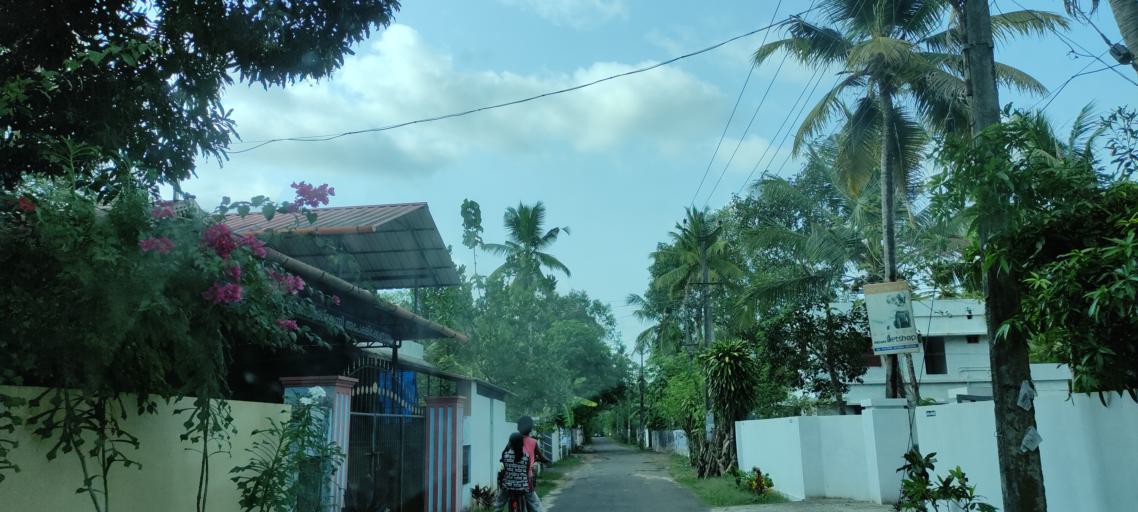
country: IN
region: Kerala
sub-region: Alappuzha
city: Vayalar
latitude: 9.6815
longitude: 76.3256
